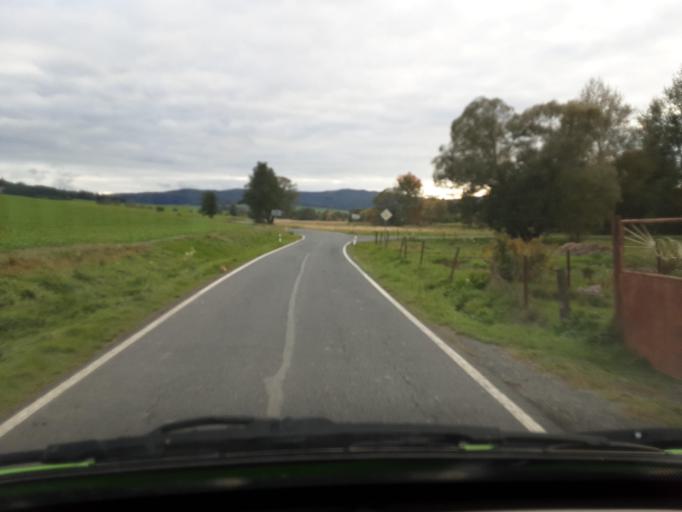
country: CZ
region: Plzensky
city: Janovice nad Uhlavou
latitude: 49.4127
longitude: 13.1630
